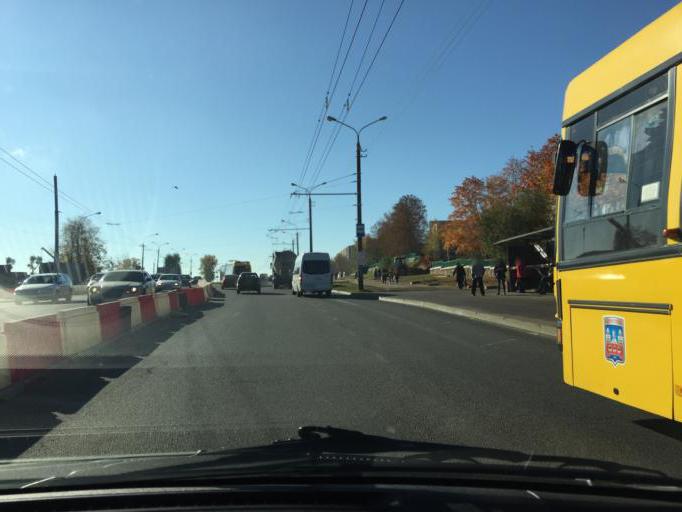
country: BY
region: Minsk
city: Syenitsa
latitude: 53.8523
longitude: 27.5374
